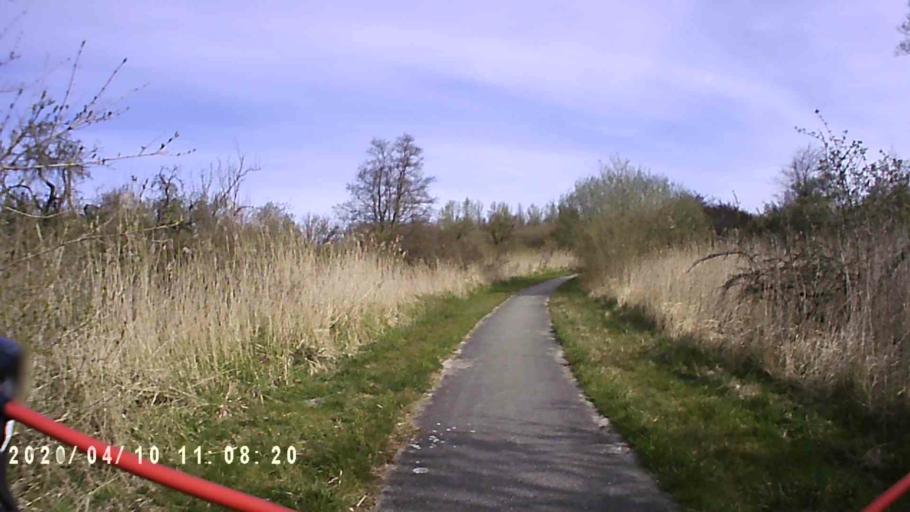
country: NL
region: Groningen
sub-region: Gemeente De Marne
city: Ulrum
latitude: 53.3909
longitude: 6.2412
